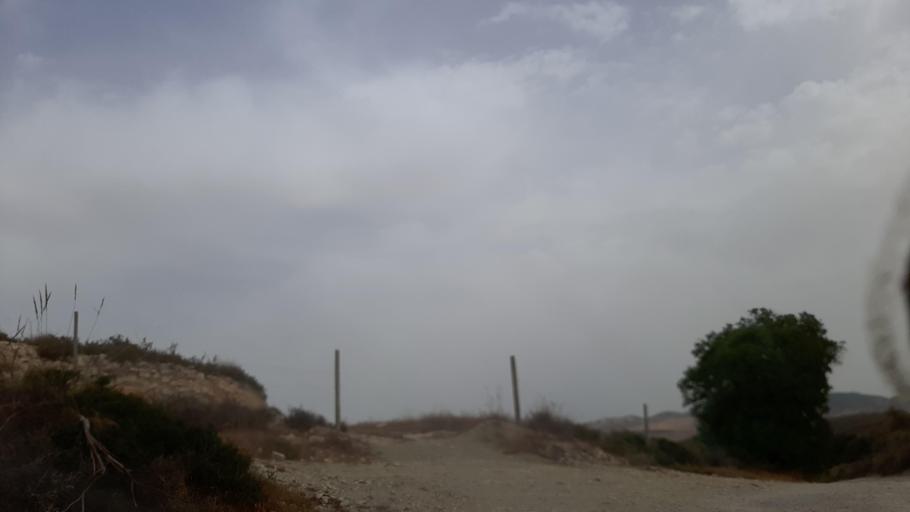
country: TN
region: Tunis
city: La Mohammedia
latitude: 36.5667
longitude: 10.1449
